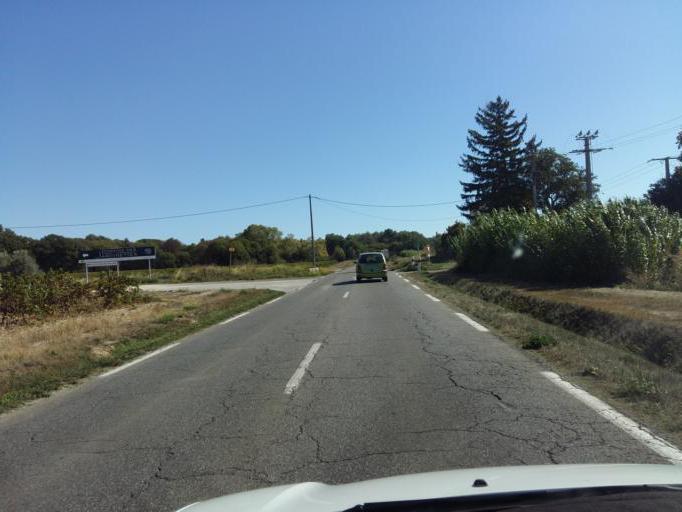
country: FR
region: Provence-Alpes-Cote d'Azur
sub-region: Departement du Vaucluse
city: Villelaure
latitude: 43.7026
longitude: 5.4504
